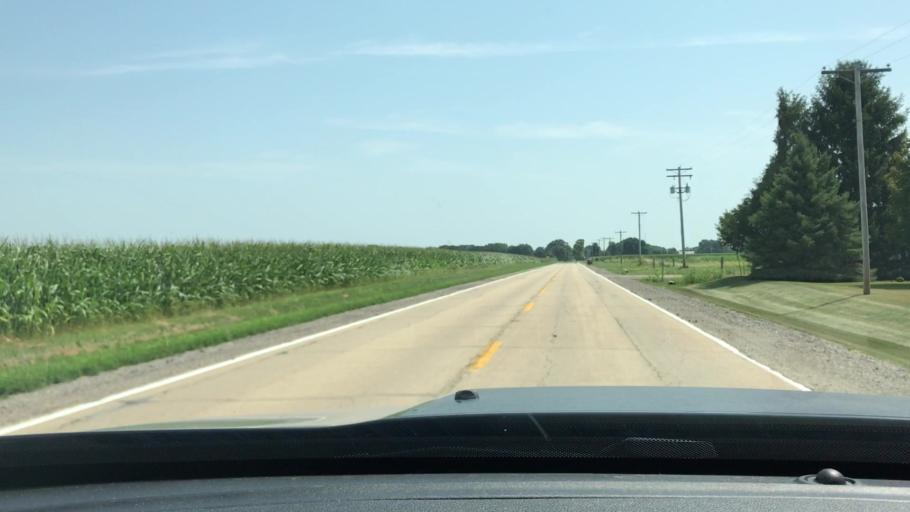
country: US
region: Illinois
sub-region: LaSalle County
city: Sheridan
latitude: 41.4853
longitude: -88.7857
